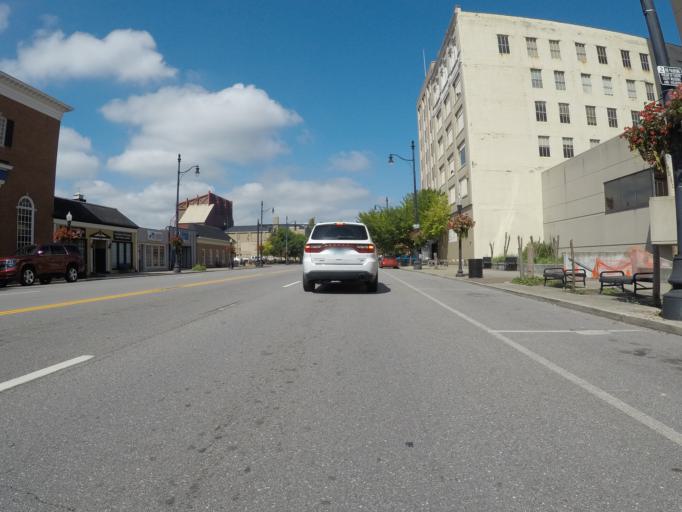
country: US
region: Kentucky
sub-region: Boyd County
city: Ashland
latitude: 38.4795
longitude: -82.6412
